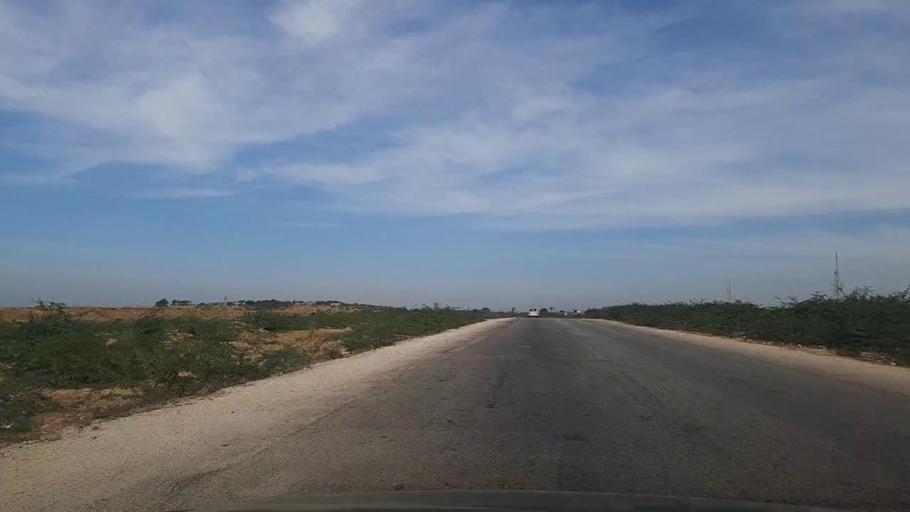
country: PK
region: Sindh
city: Daro Mehar
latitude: 24.8894
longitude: 68.0575
